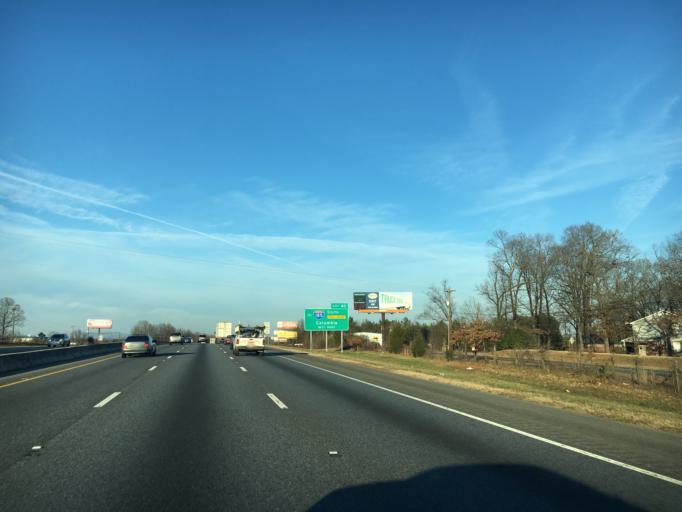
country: US
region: South Carolina
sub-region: Anderson County
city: Powdersville
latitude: 34.7660
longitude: -82.4710
